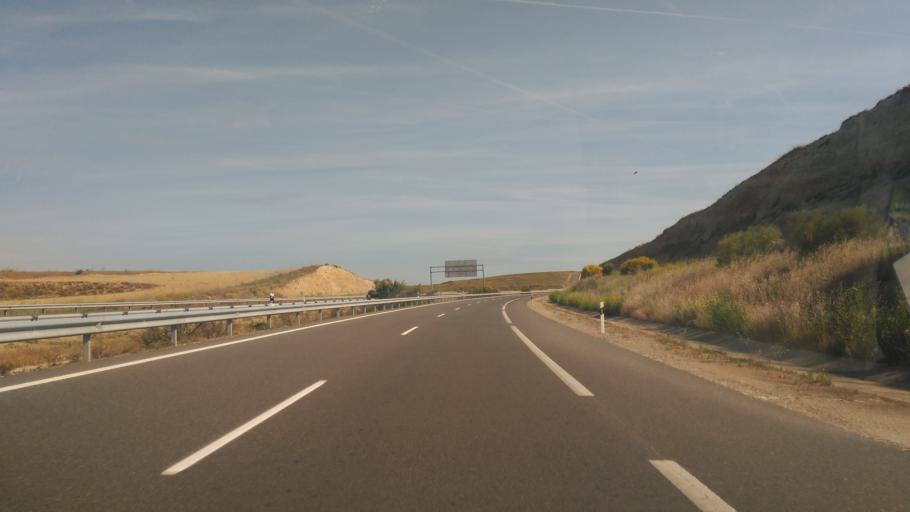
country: ES
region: Castille and Leon
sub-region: Provincia de Salamanca
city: Villamayor
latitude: 41.0046
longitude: -5.6787
